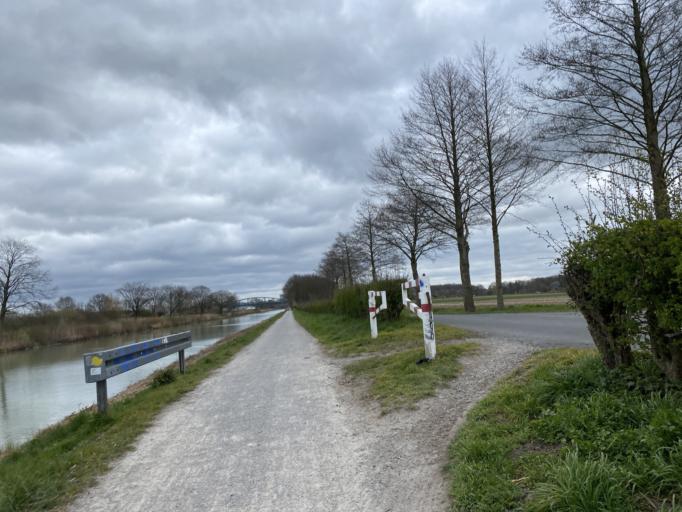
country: DE
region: North Rhine-Westphalia
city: Ahlen
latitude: 51.6900
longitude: 7.9132
